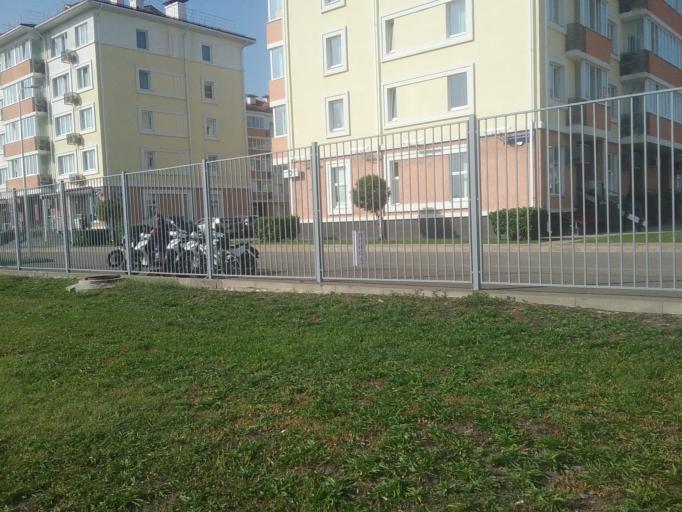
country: RU
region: Krasnodarskiy
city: Adler
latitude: 43.3998
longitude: 39.9799
